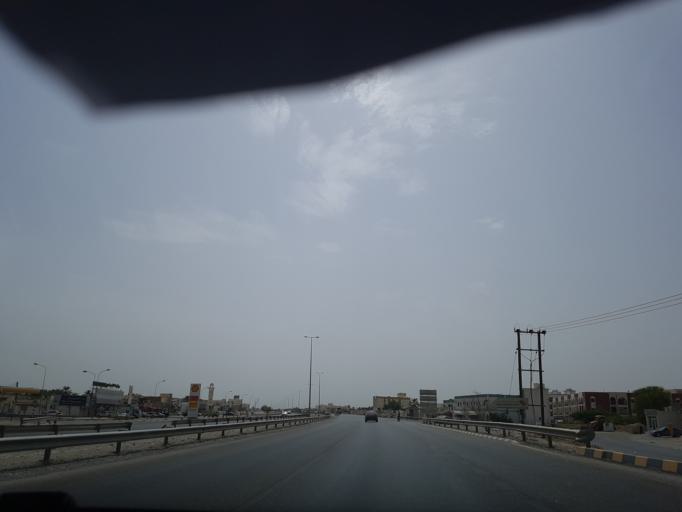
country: OM
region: Al Batinah
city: As Suwayq
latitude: 23.7449
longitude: 57.6210
